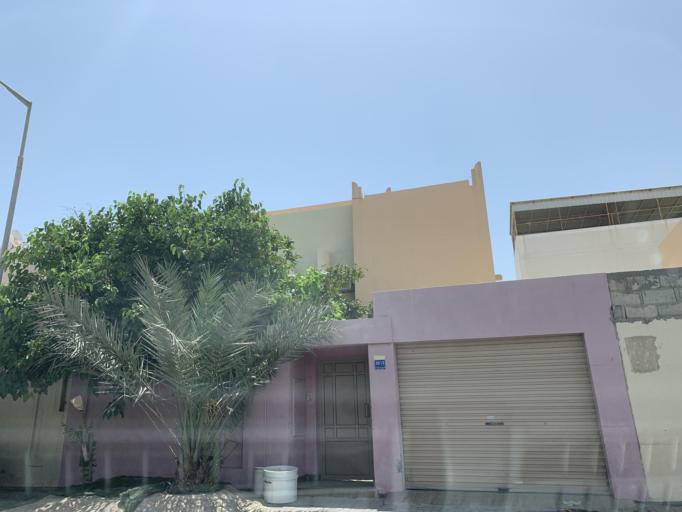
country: BH
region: Northern
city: Sitrah
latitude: 26.1421
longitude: 50.5904
